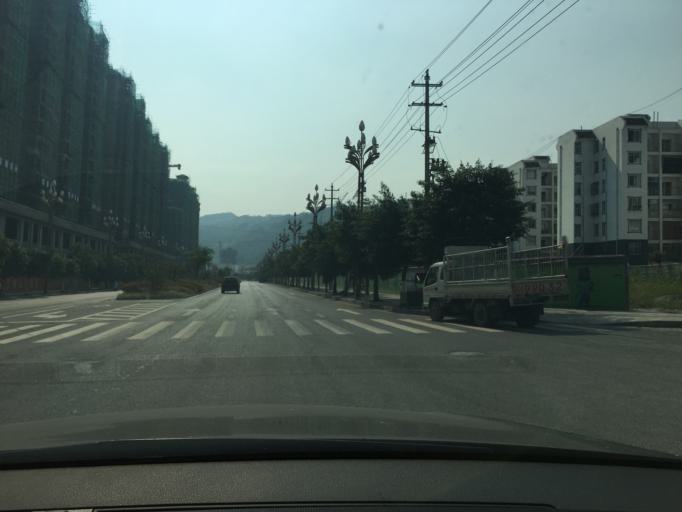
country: CN
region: Guangxi Zhuangzu Zizhiqu
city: Xinzhou
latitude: 24.9949
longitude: 105.7891
